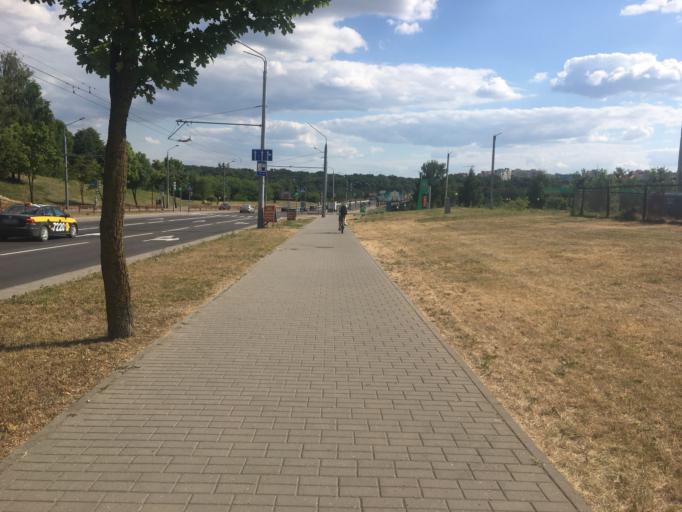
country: BY
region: Grodnenskaya
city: Hrodna
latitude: 53.6651
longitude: 23.8604
